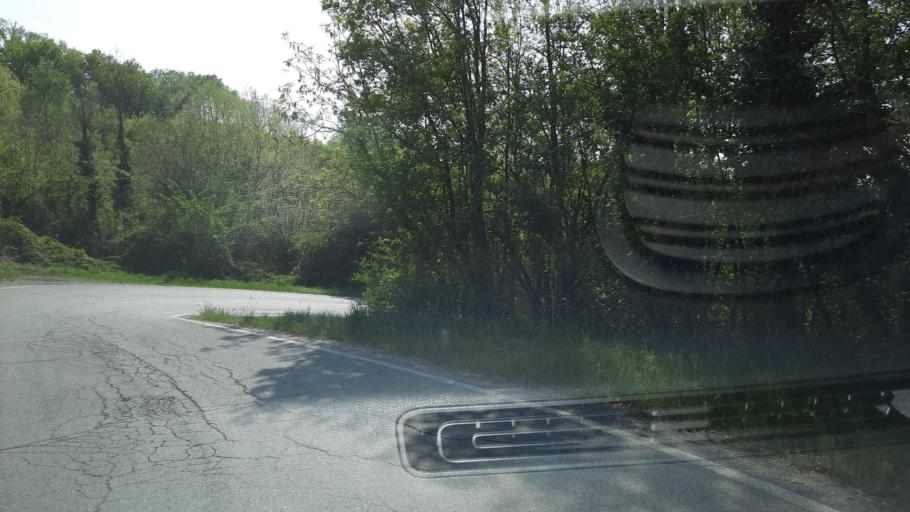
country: IT
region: Piedmont
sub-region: Provincia di Torino
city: Verrua Savoia
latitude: 45.1714
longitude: 8.1014
